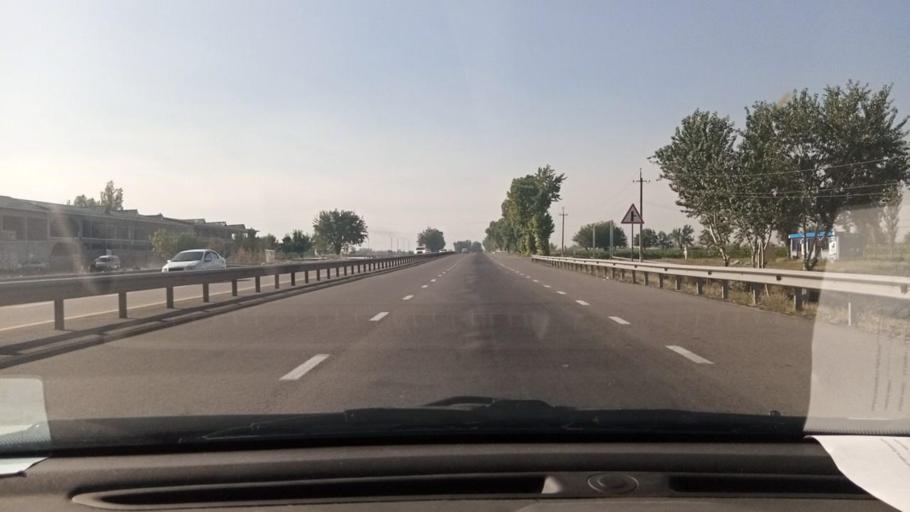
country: UZ
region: Toshkent Shahri
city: Bektemir
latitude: 41.1501
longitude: 69.4277
